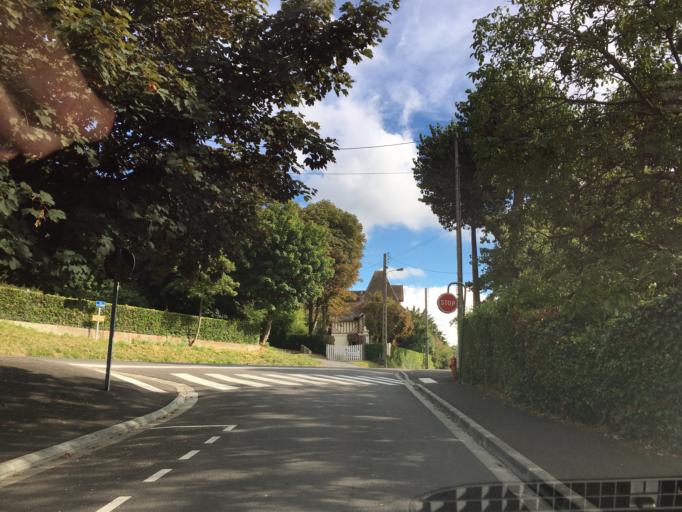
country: FR
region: Lower Normandy
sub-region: Departement du Calvados
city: Houlgate
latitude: 49.3032
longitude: -0.0700
